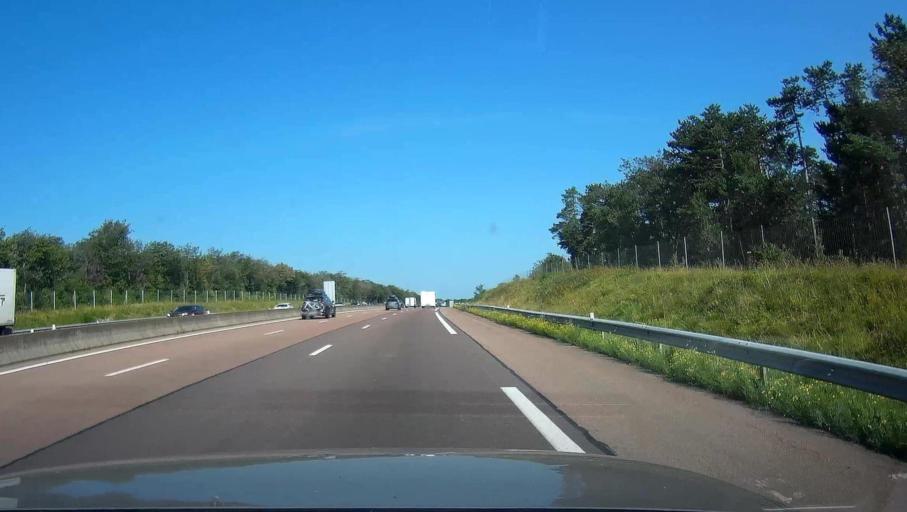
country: FR
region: Bourgogne
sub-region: Departement de la Cote-d'Or
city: Selongey
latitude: 47.6150
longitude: 5.1829
